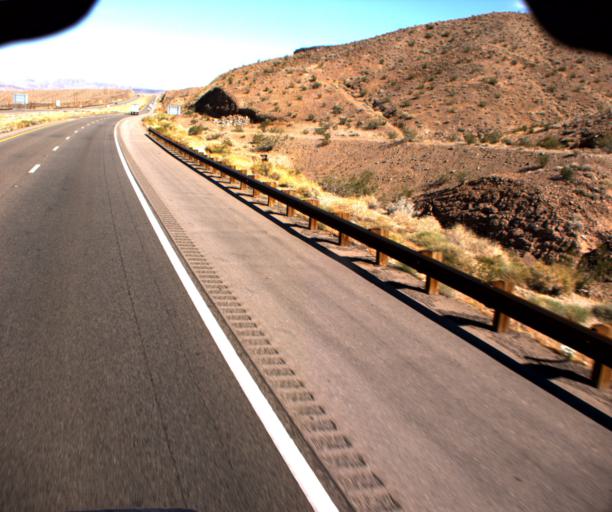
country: US
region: Nevada
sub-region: Clark County
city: Boulder City
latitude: 35.8614
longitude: -114.6007
